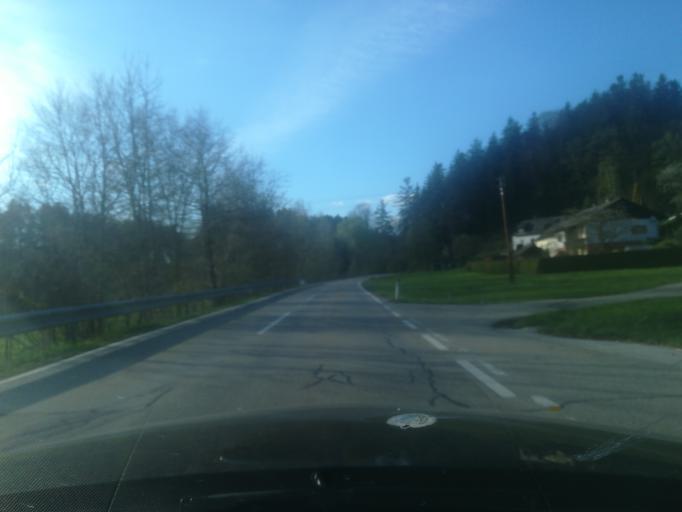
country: AT
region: Upper Austria
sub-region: Politischer Bezirk Perg
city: Bad Kreuzen
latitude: 48.2346
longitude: 14.8396
